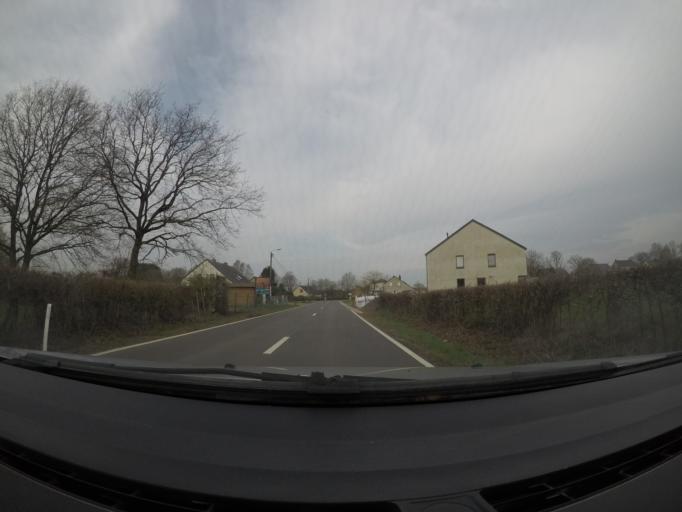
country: BE
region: Wallonia
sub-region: Province du Luxembourg
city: Tintigny
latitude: 49.7038
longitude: 5.4303
